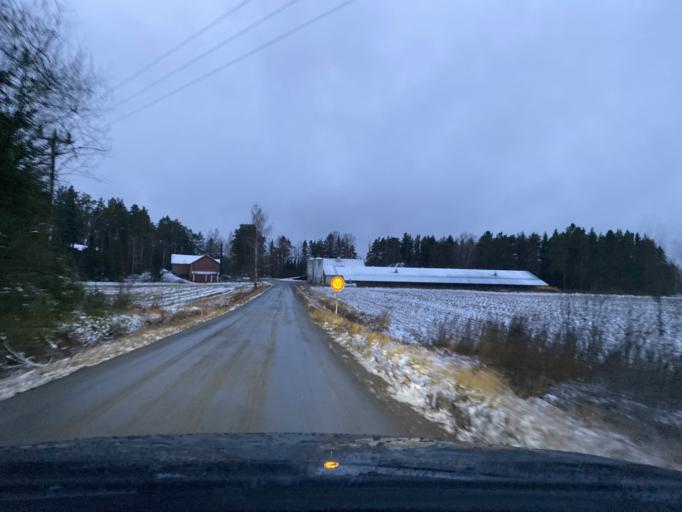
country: FI
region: Pirkanmaa
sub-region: Lounais-Pirkanmaa
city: Punkalaidun
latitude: 61.1447
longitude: 22.9661
